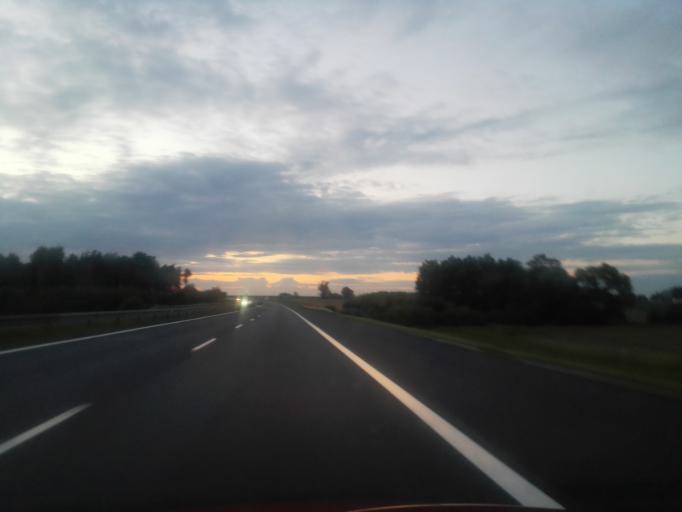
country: PL
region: Lodz Voivodeship
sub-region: Piotrkow Trybunalski
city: Piotrkow Trybunalski
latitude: 51.4494
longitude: 19.6418
